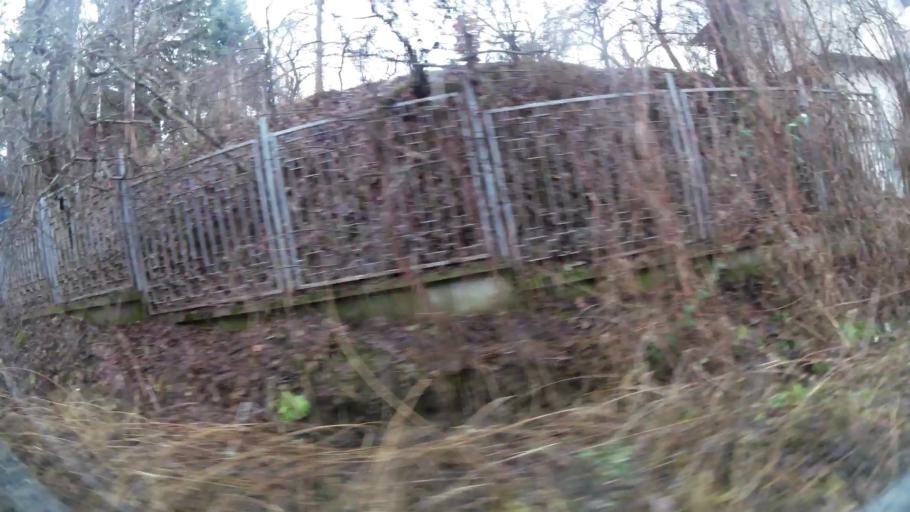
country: BG
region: Sofia-Capital
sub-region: Stolichna Obshtina
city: Sofia
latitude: 42.6027
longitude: 23.3874
